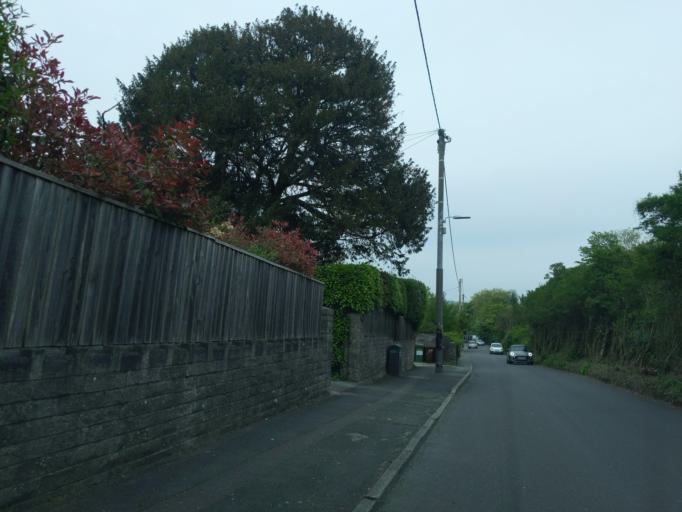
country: GB
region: England
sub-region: Devon
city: Plympton
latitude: 50.3914
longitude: -4.0569
